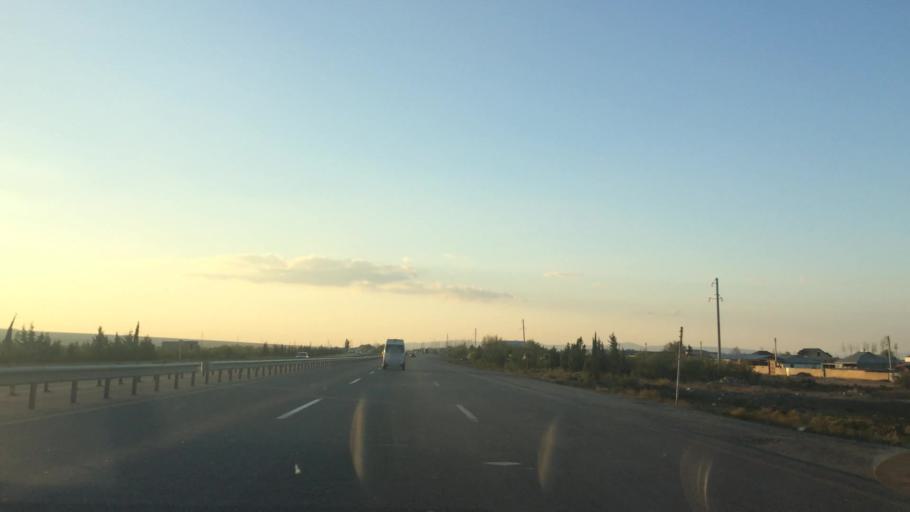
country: AZ
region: Haciqabul
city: Haciqabul
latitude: 40.0046
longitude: 49.1649
